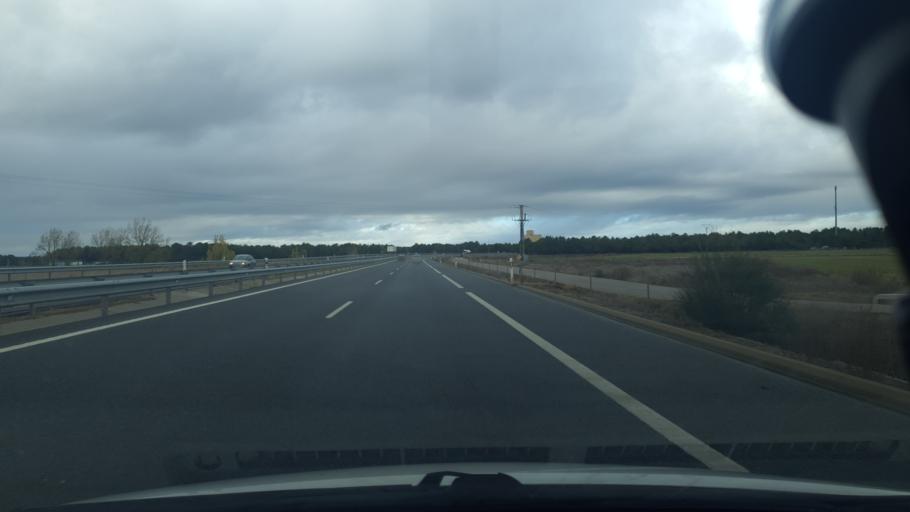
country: ES
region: Castille and Leon
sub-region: Provincia de Segovia
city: Sanchonuno
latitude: 41.3229
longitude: -4.3131
